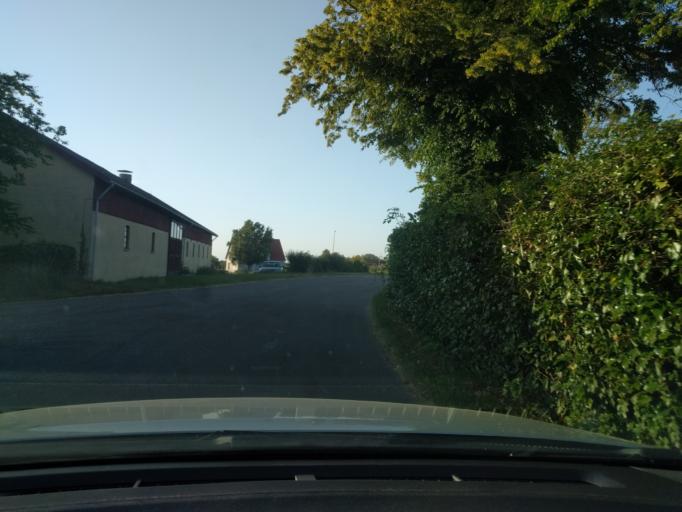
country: DK
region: Zealand
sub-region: Vordingborg Kommune
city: Stege
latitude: 54.9659
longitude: 12.2317
